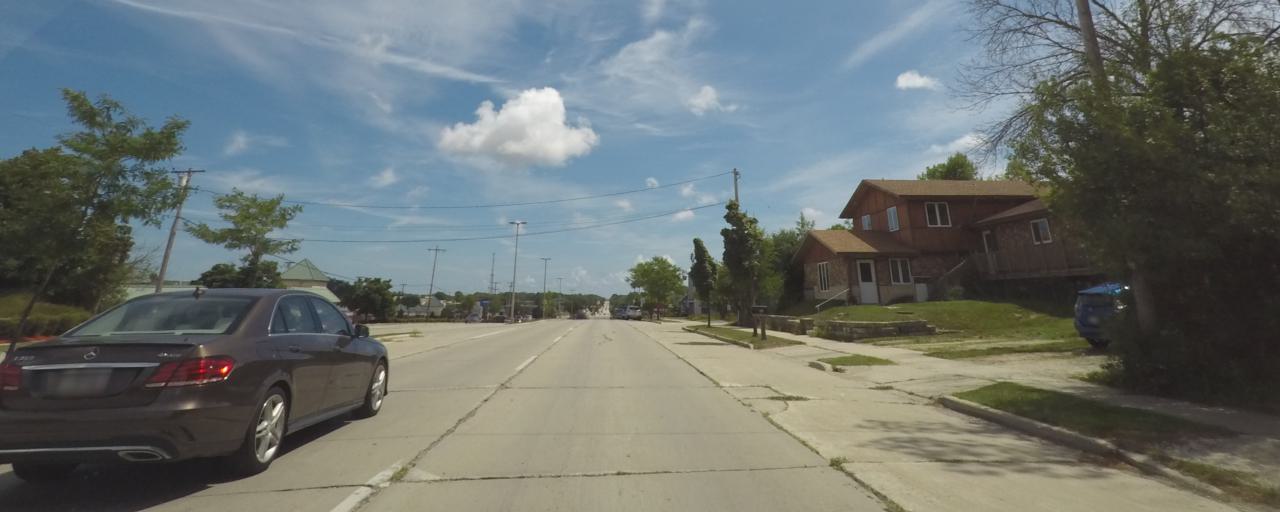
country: US
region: Wisconsin
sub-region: Milwaukee County
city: Greenfield
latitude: 42.9593
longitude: -87.9940
